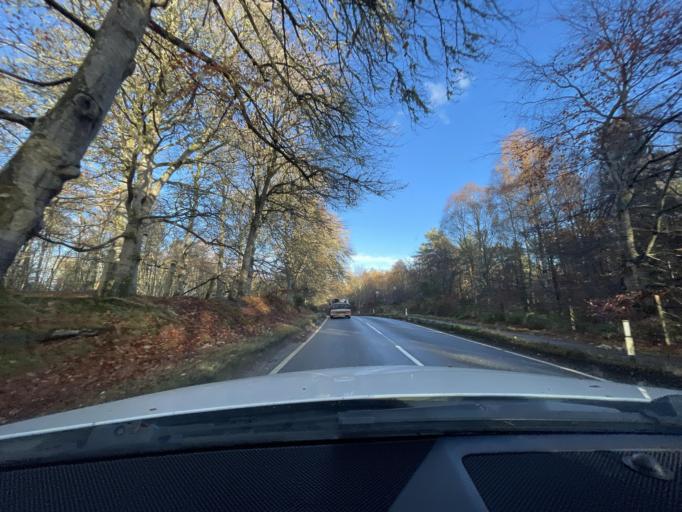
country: GB
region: Scotland
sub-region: Highland
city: Inverness
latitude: 57.4363
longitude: -4.2685
